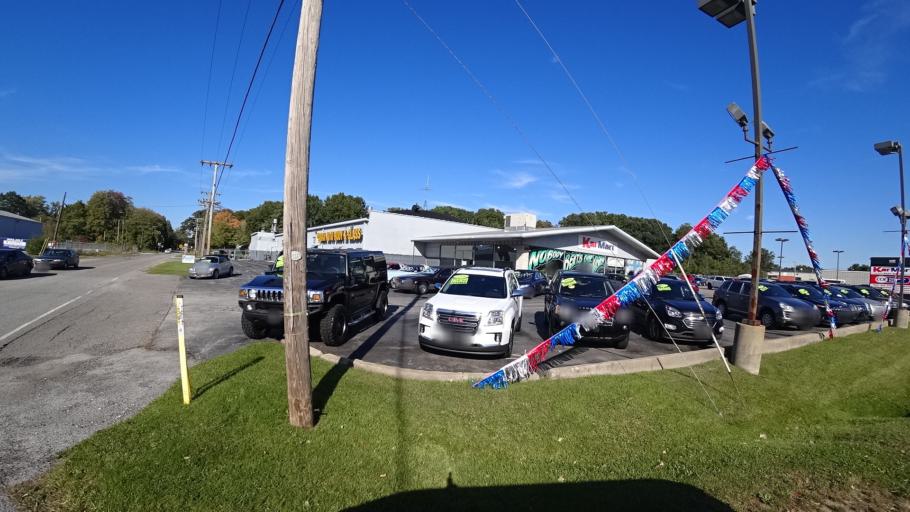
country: US
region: Indiana
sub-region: LaPorte County
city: Trail Creek
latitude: 41.7046
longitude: -86.8527
